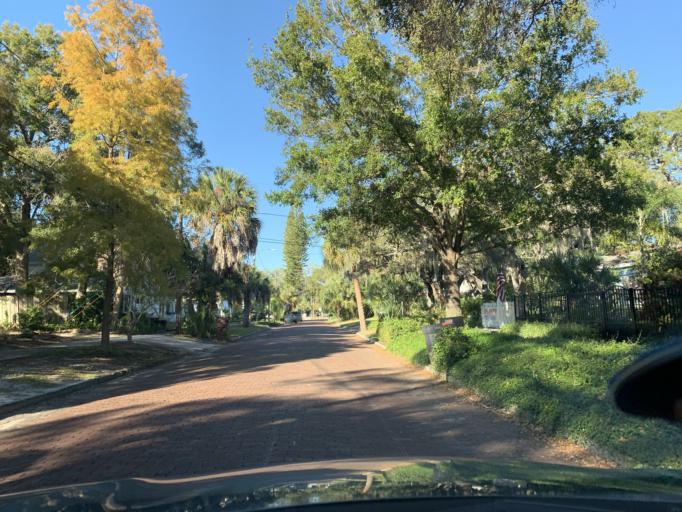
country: US
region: Florida
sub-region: Pinellas County
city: Gulfport
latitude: 27.7399
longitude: -82.7039
